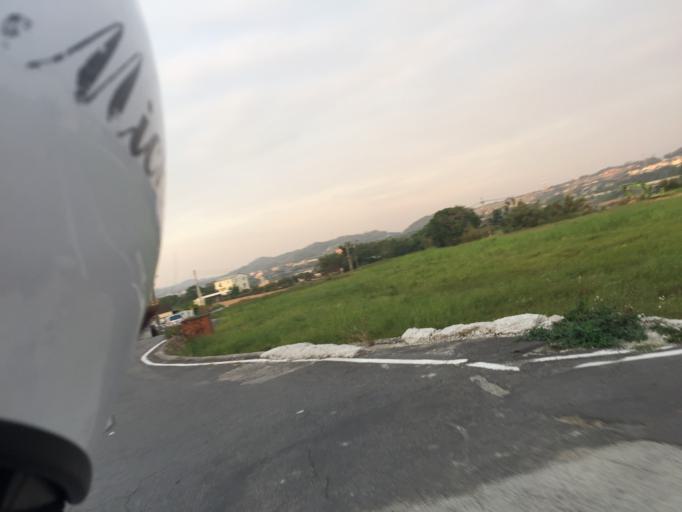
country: TW
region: Taiwan
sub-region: Miaoli
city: Miaoli
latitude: 24.4891
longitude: 120.7757
